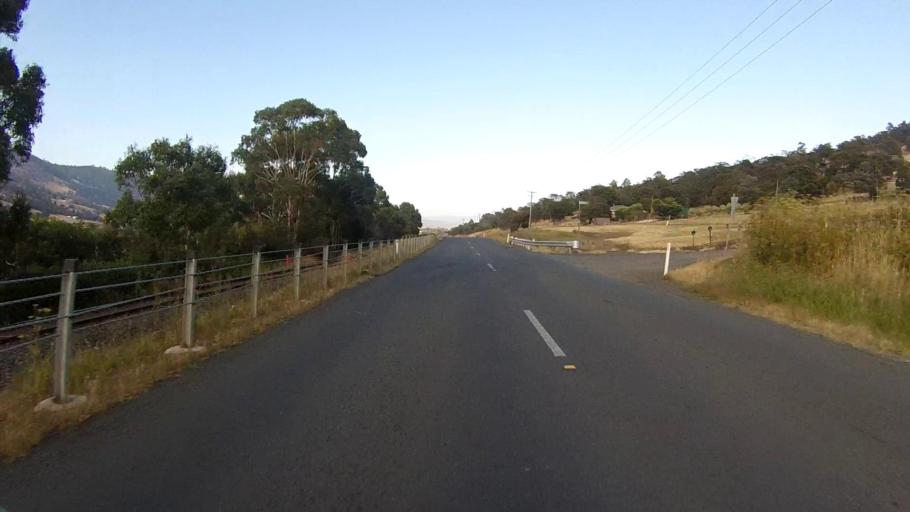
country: AU
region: Tasmania
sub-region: Glenorchy
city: Granton
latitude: -42.7517
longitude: 147.1496
